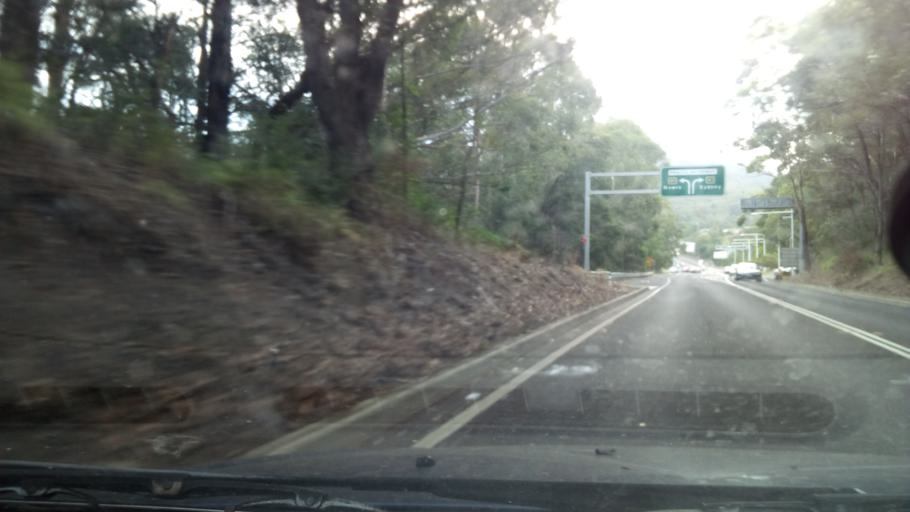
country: AU
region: New South Wales
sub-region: Wollongong
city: Mount Ousley
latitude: -34.4020
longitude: 150.8829
